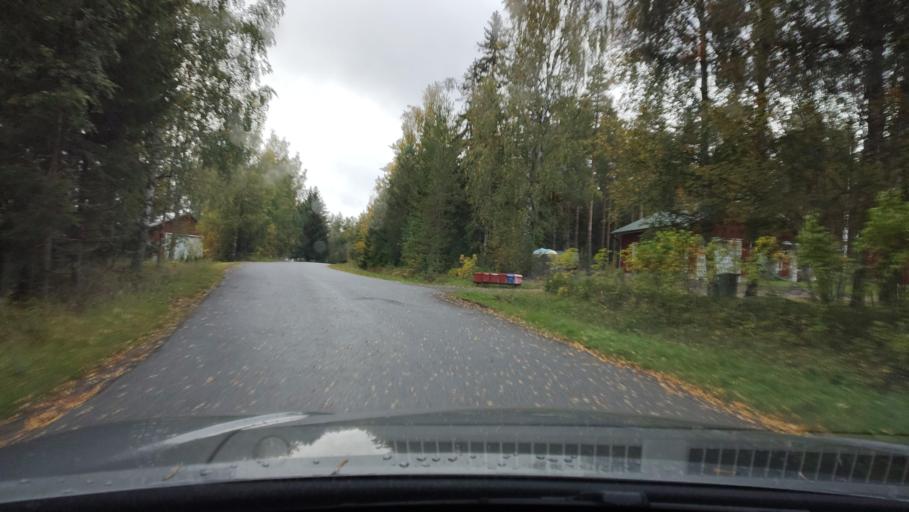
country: FI
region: Ostrobothnia
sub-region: Sydosterbotten
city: Kristinestad
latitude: 62.2638
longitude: 21.4655
